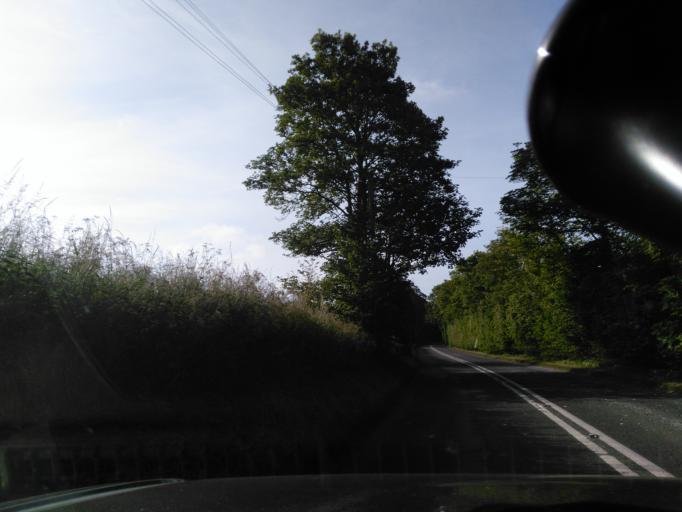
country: GB
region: England
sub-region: Wiltshire
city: Market Lavington
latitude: 51.2549
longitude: -1.9865
